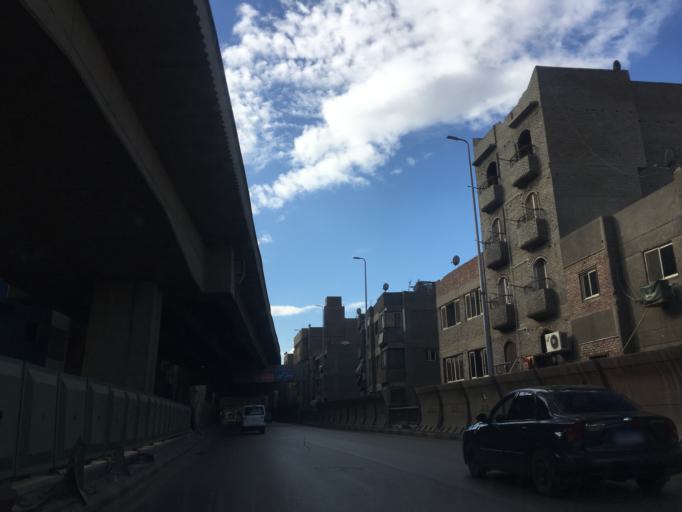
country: EG
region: Al Jizah
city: Al Jizah
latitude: 30.0305
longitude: 31.1828
